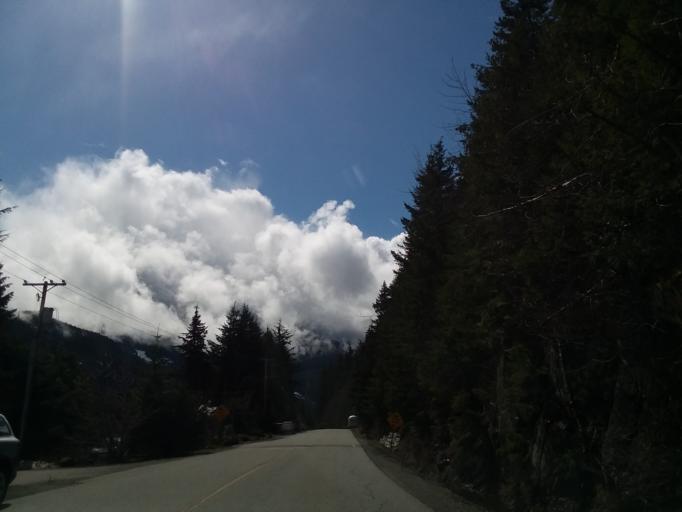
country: CA
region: British Columbia
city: Whistler
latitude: 50.1175
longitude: -122.9864
